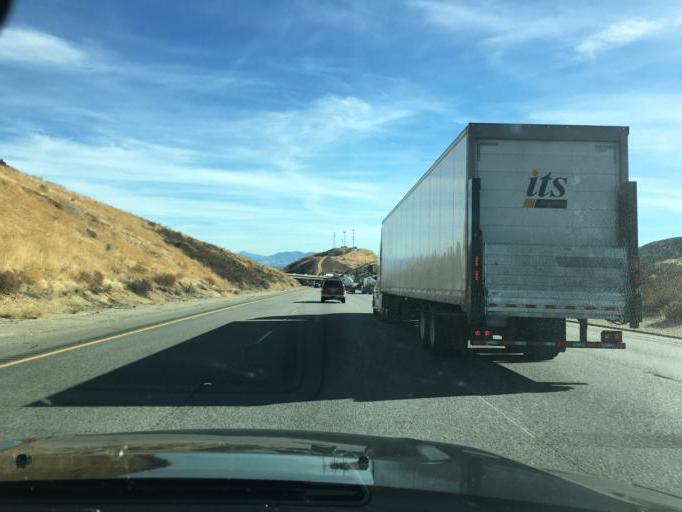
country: US
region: California
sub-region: Los Angeles County
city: Castaic
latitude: 34.5570
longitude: -118.6752
